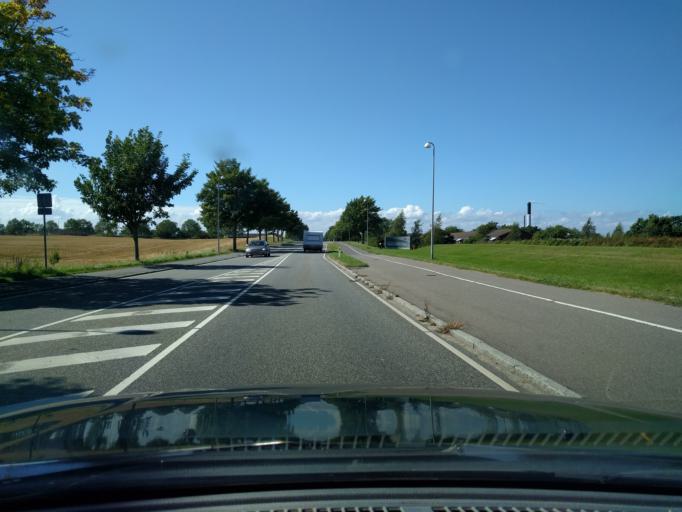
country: DK
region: Zealand
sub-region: Slagelse Kommune
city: Korsor
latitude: 55.3244
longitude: 11.1731
